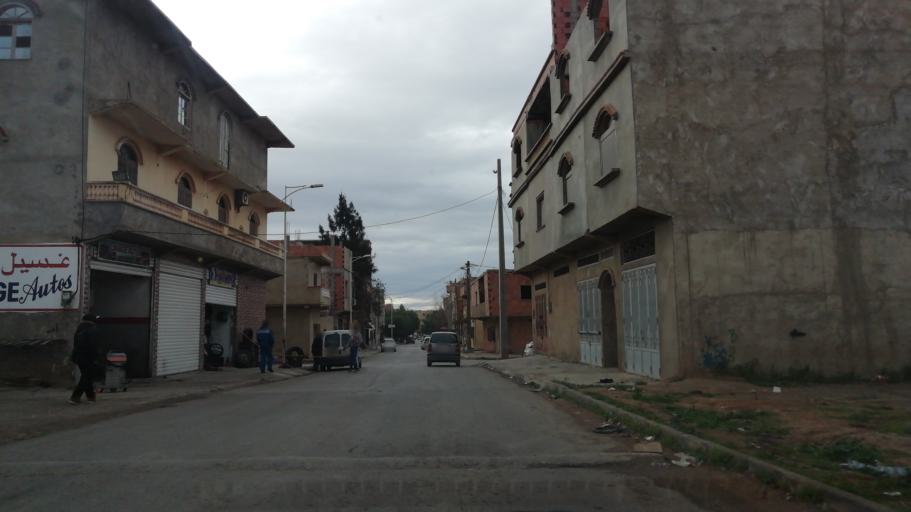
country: DZ
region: Oran
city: Oran
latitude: 35.6875
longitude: -0.5970
